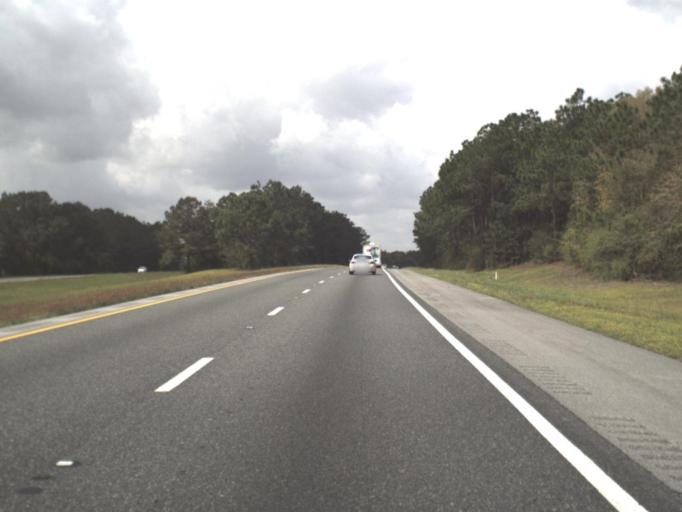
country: US
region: Florida
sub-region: Okaloosa County
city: Crestview
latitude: 30.7156
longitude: -86.6149
